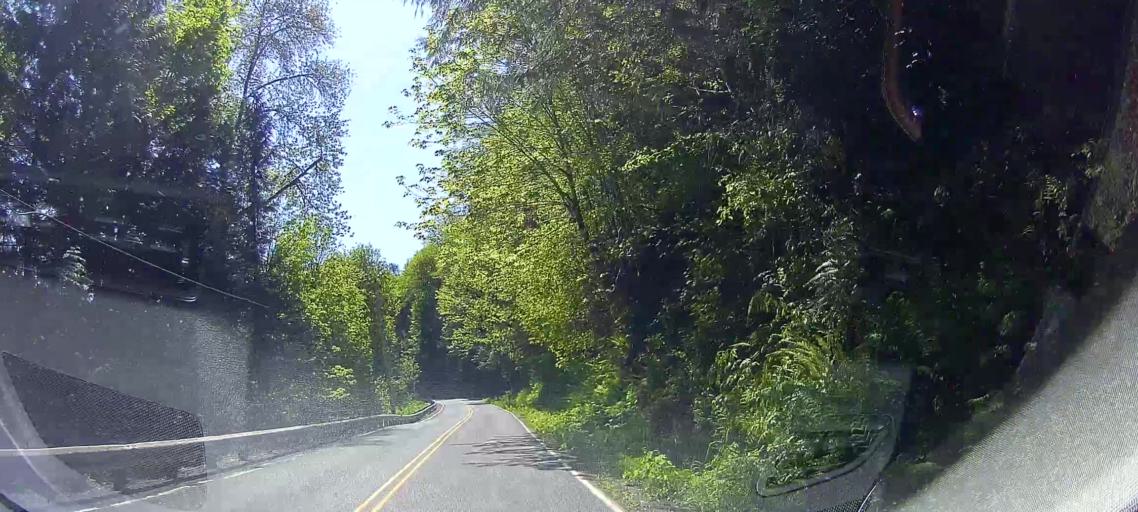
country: US
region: Washington
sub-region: Snohomish County
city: Darrington
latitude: 48.4774
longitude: -121.6474
